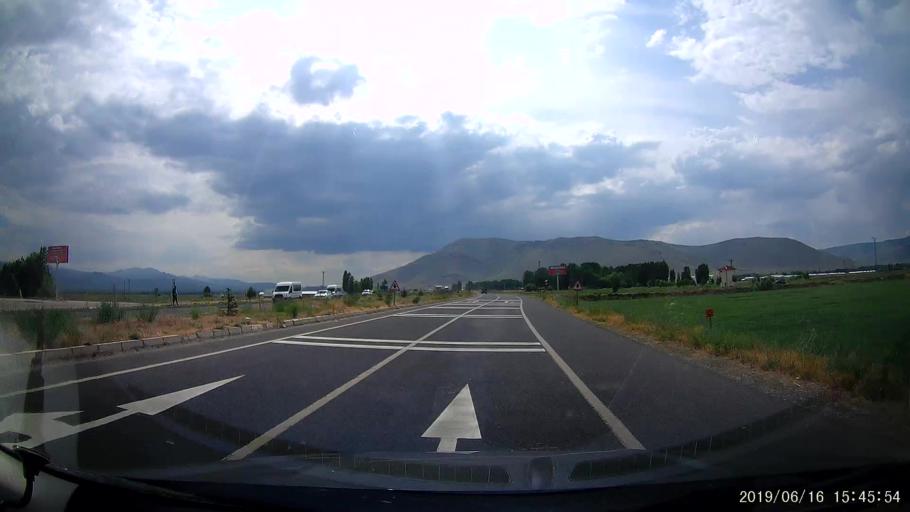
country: TR
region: Erzurum
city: Pasinler
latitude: 39.9895
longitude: 41.7558
